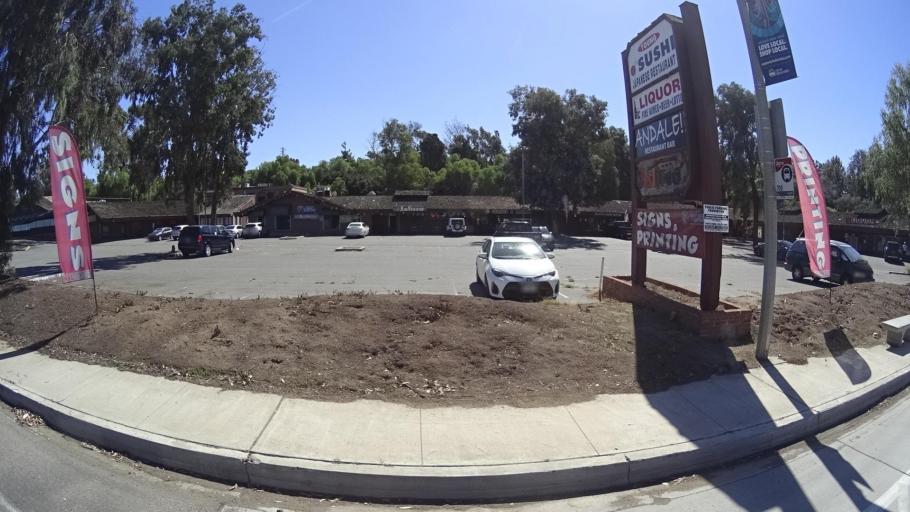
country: US
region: California
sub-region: San Diego County
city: Bonita
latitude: 32.6586
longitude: -117.0396
